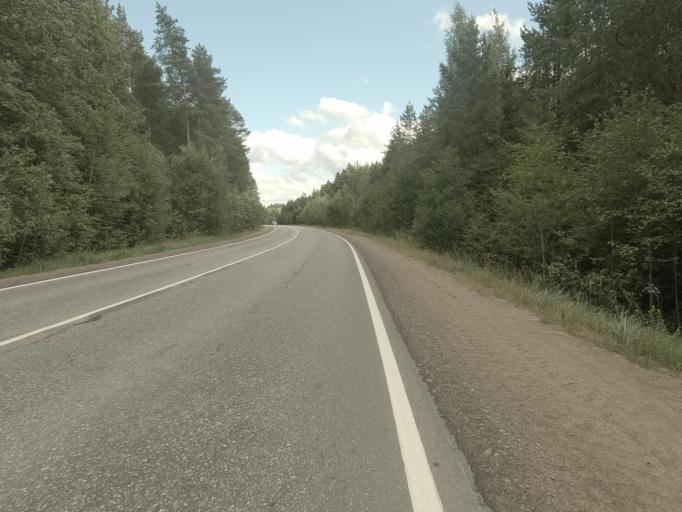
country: RU
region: Leningrad
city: Shcheglovo
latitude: 60.0102
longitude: 30.8566
